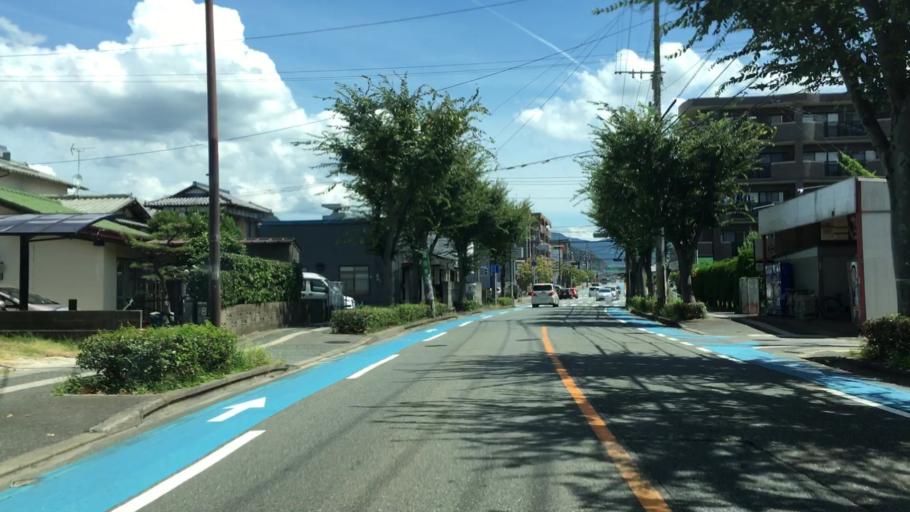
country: JP
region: Fukuoka
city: Onojo
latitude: 33.5430
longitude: 130.4778
